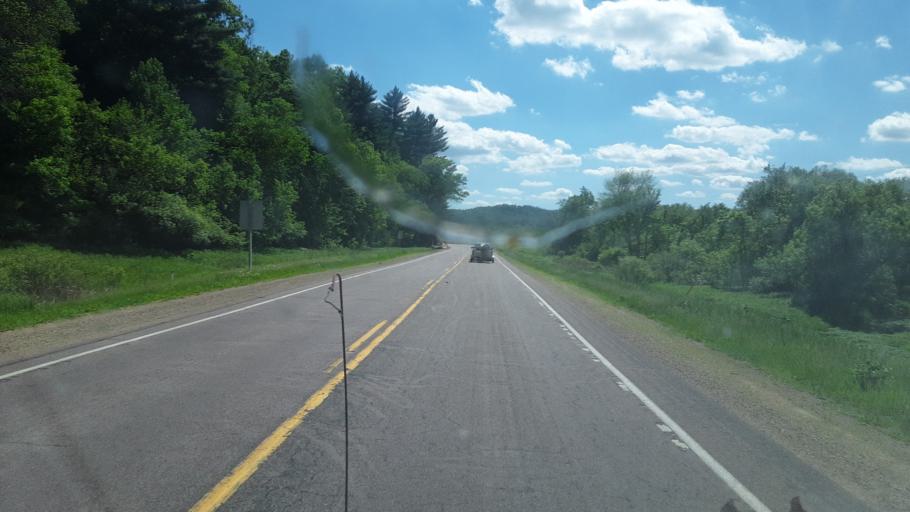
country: US
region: Wisconsin
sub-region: Richland County
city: Richland Center
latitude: 43.3820
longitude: -90.2544
